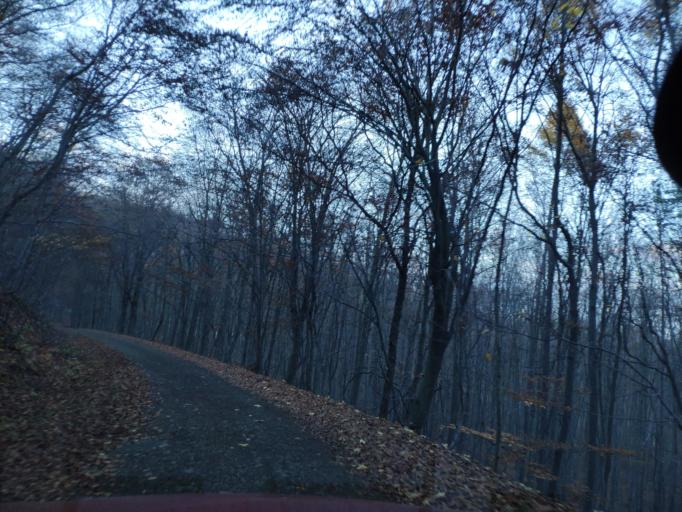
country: SK
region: Kosicky
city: Secovce
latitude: 48.5844
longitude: 21.5073
